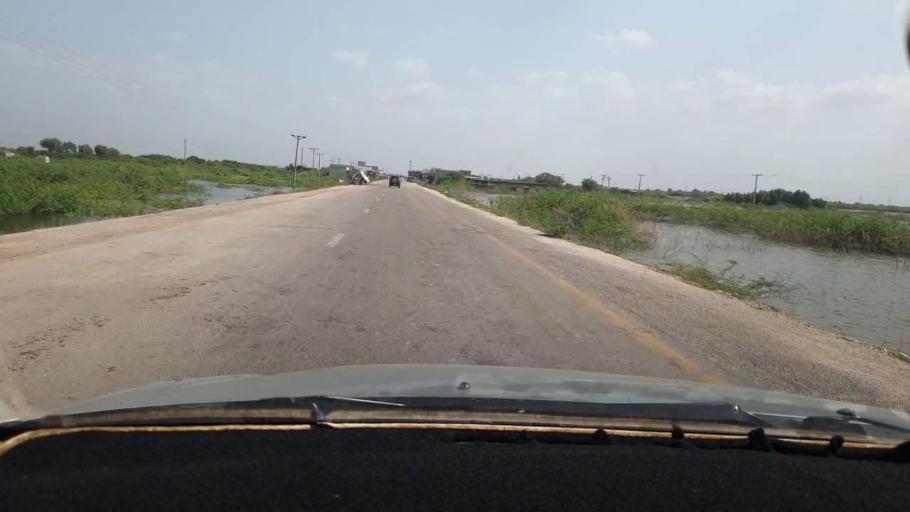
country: PK
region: Sindh
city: Naukot
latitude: 24.9049
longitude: 69.3289
